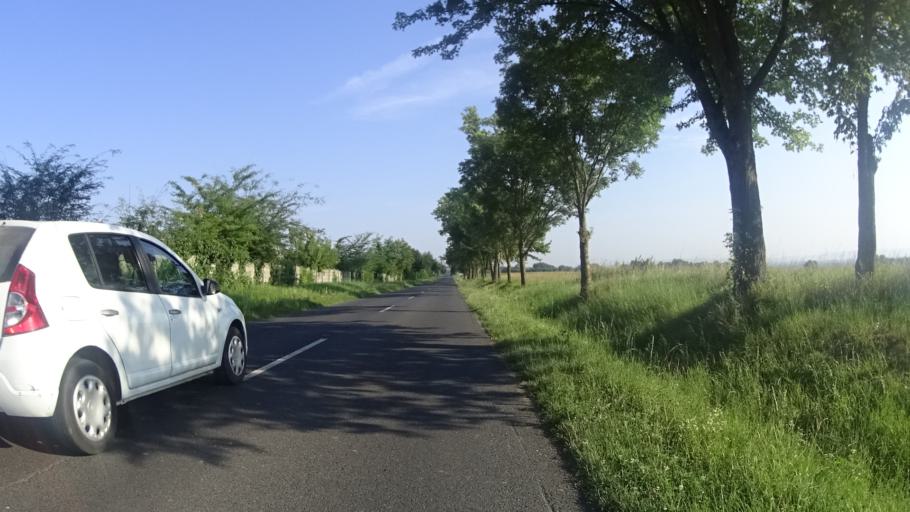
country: HU
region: Zala
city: Sarmellek
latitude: 46.6873
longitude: 17.1688
